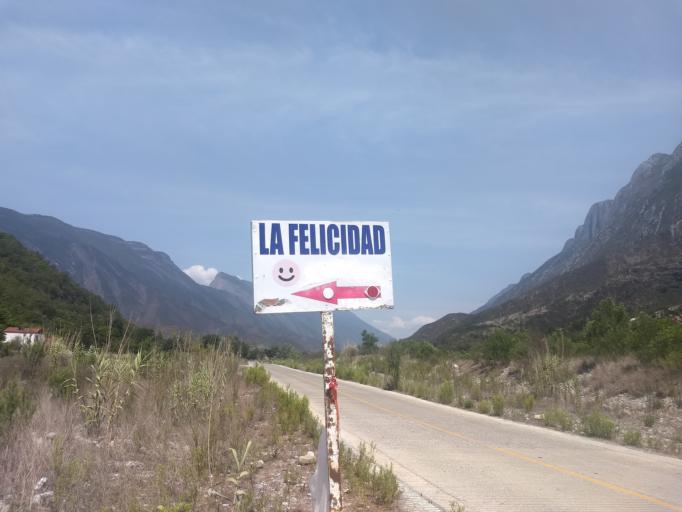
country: MX
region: Nuevo Leon
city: Santiago
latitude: 25.3928
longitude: -100.2790
